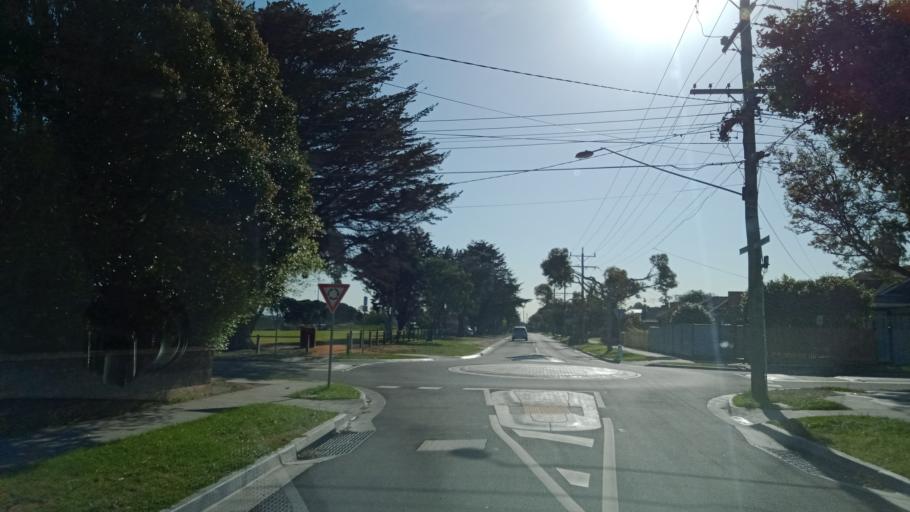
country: AU
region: Victoria
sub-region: Kingston
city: Edithvale
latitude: -38.0379
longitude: 145.1181
